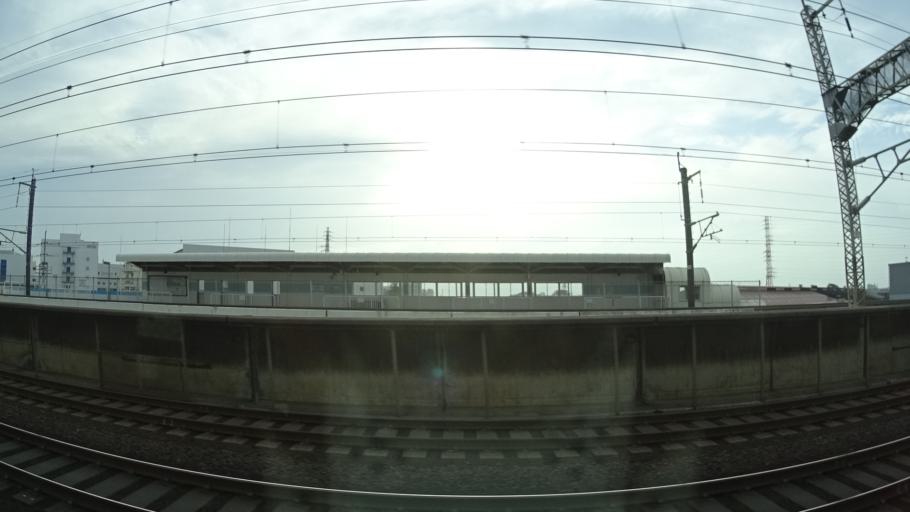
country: JP
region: Saitama
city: Ageoshimo
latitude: 35.9582
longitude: 139.6212
